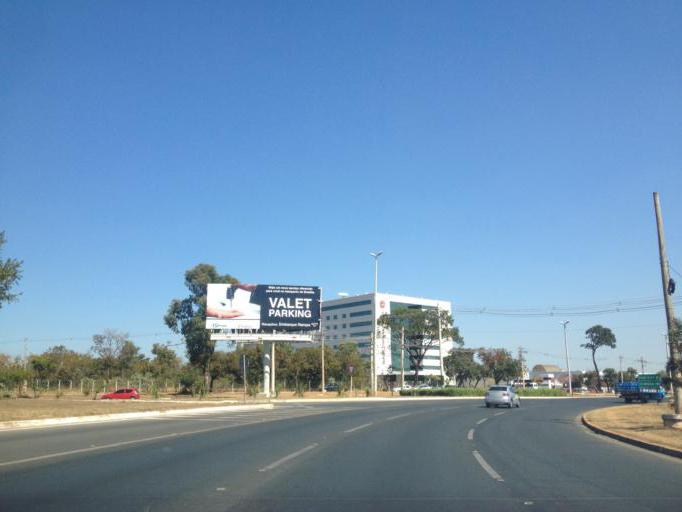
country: BR
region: Federal District
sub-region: Brasilia
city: Brasilia
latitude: -15.8697
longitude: -47.9255
